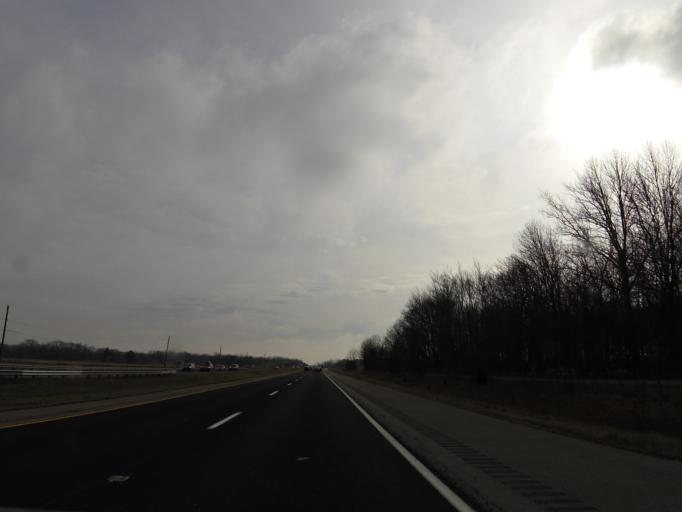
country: US
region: Indiana
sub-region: Hancock County
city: New Palestine
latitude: 39.6554
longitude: -85.9300
